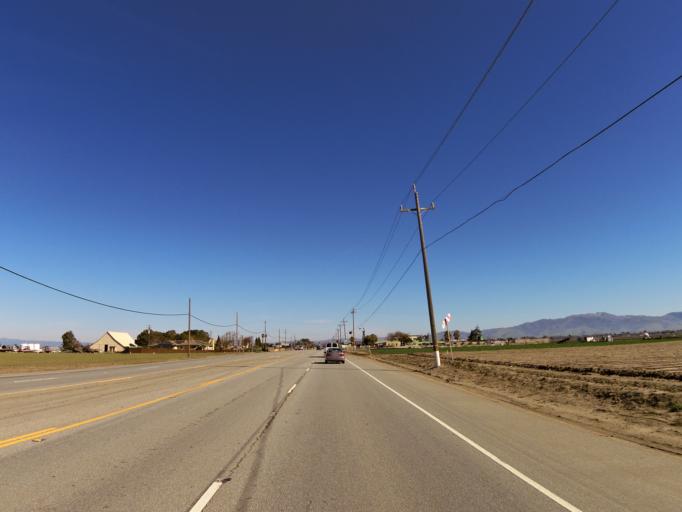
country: US
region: California
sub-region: Monterey County
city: Salinas
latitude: 36.6403
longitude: -121.6658
